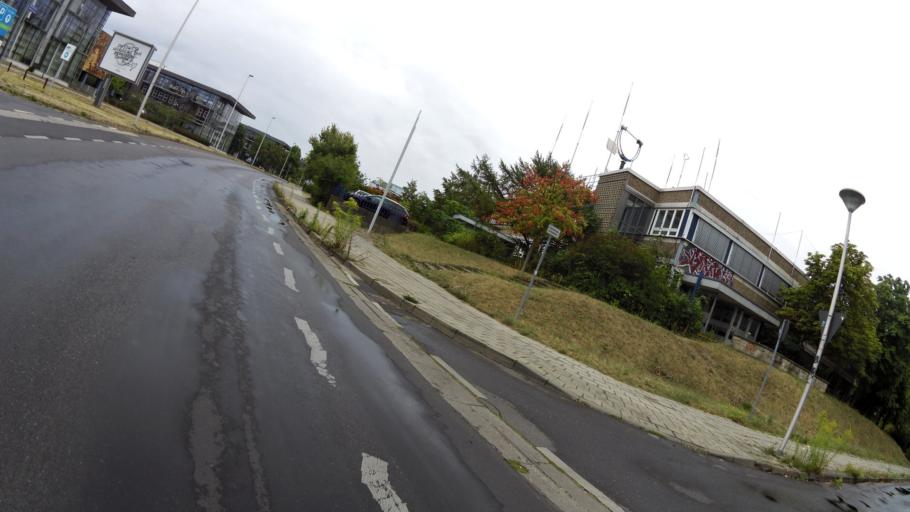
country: DE
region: Brandenburg
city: Cottbus
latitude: 51.7663
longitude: 14.3212
